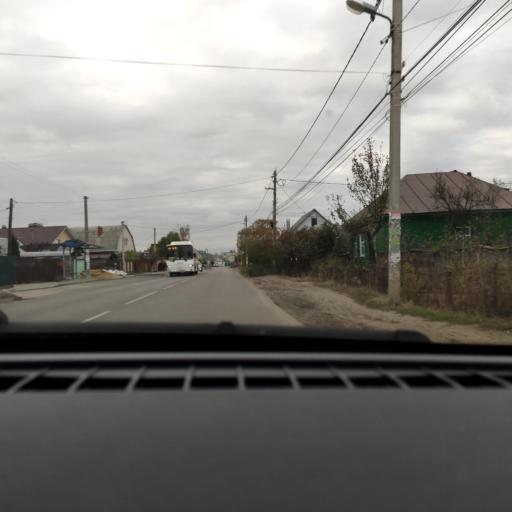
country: RU
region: Voronezj
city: Somovo
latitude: 51.7344
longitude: 39.2903
